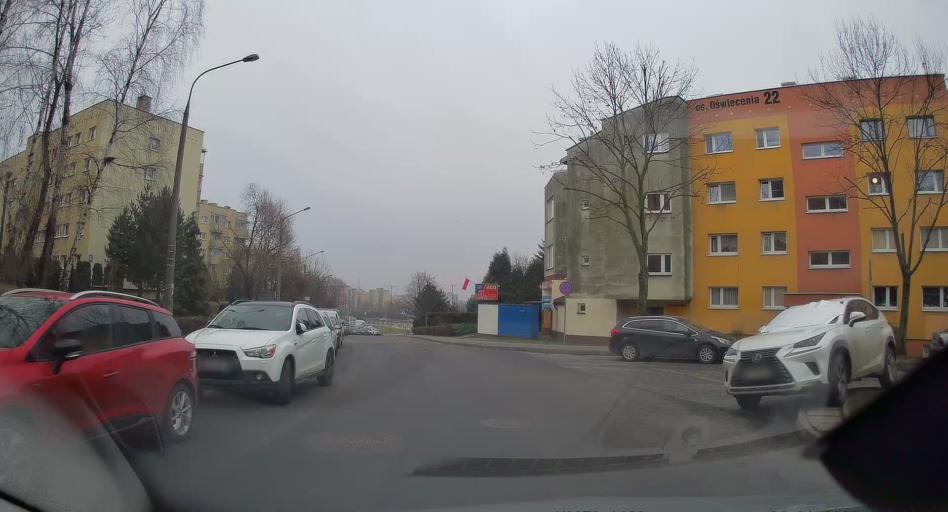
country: PL
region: Lesser Poland Voivodeship
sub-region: Krakow
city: Krakow
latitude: 50.0887
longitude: 19.9933
